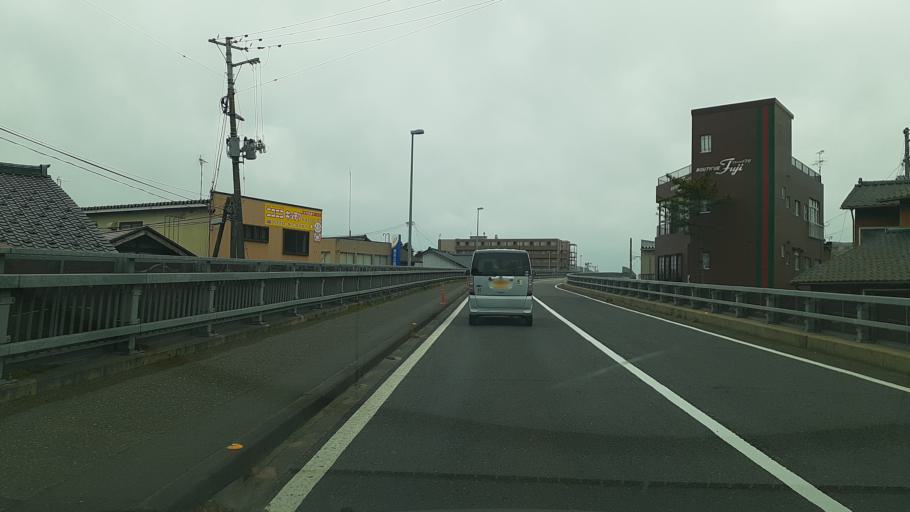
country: JP
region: Niigata
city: Niitsu-honcho
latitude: 37.7953
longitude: 139.1234
